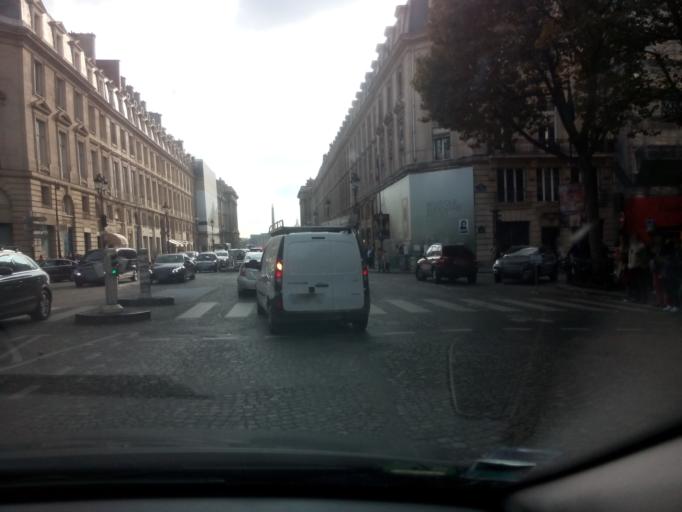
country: FR
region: Ile-de-France
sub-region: Paris
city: Paris
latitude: 48.8687
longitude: 2.3234
